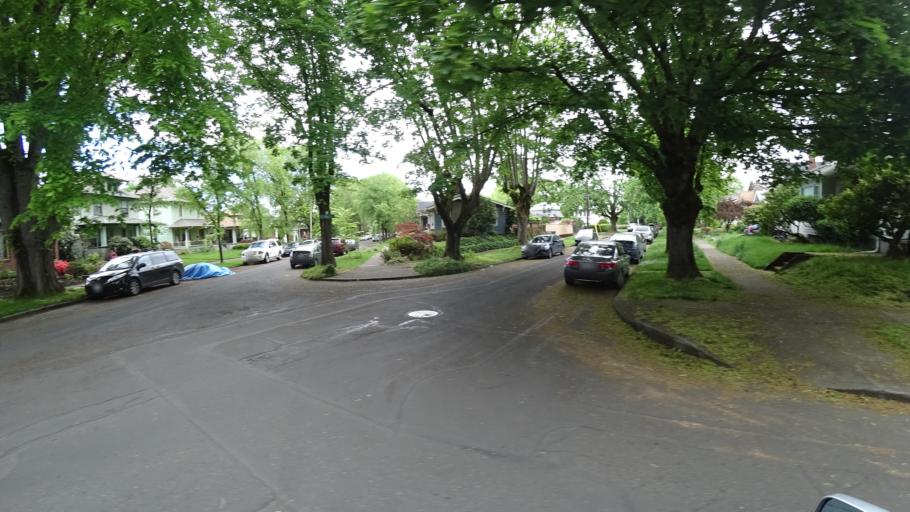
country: US
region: Oregon
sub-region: Multnomah County
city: Portland
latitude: 45.5074
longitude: -122.6525
